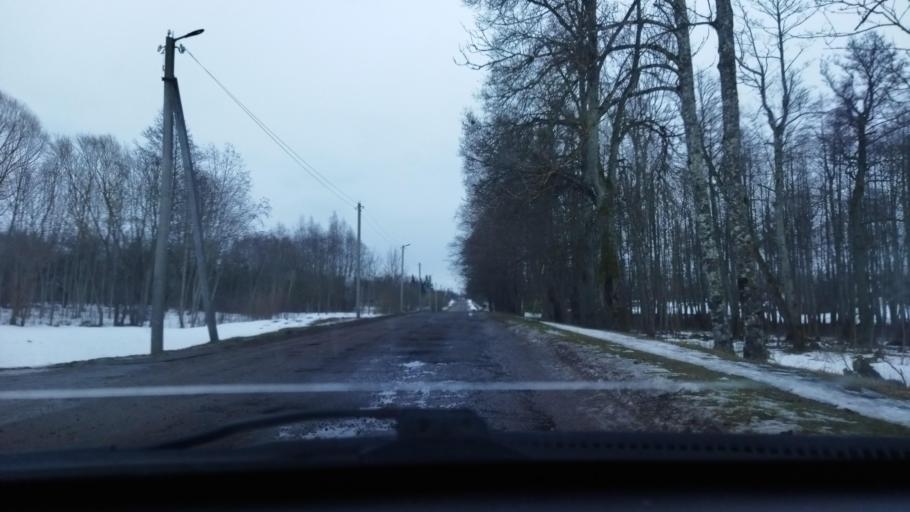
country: BY
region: Minsk
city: Svir
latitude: 54.9003
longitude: 26.4012
